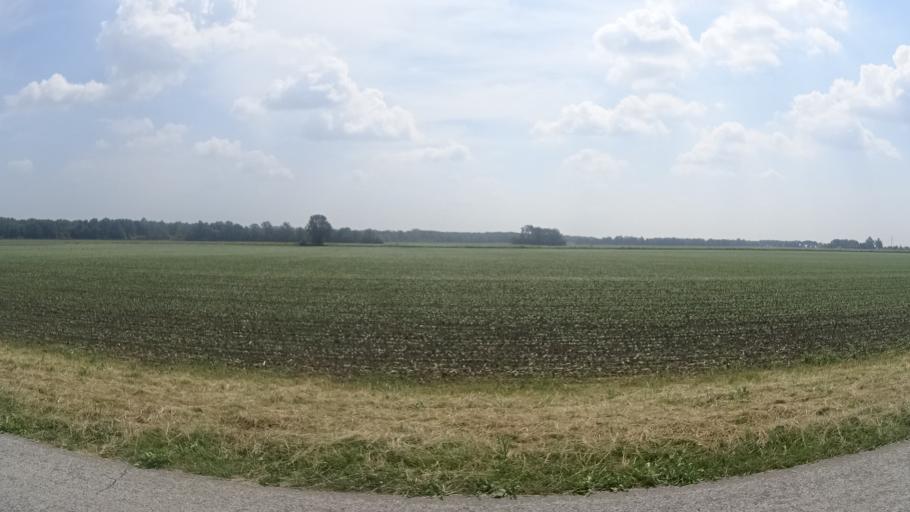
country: US
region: Ohio
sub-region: Erie County
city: Sandusky
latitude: 41.3527
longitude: -82.6943
